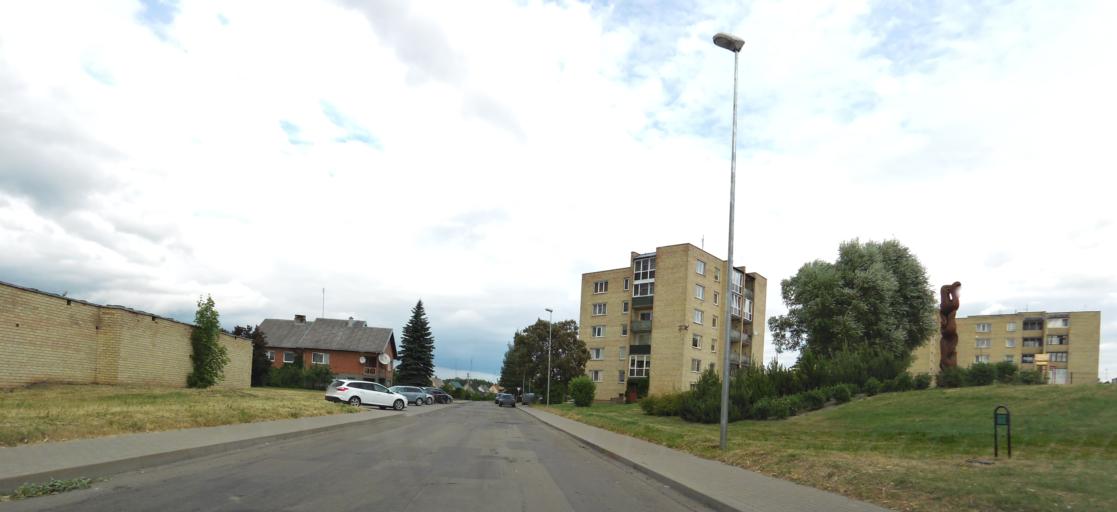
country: LT
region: Panevezys
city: Pasvalys
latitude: 56.0641
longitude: 24.4148
